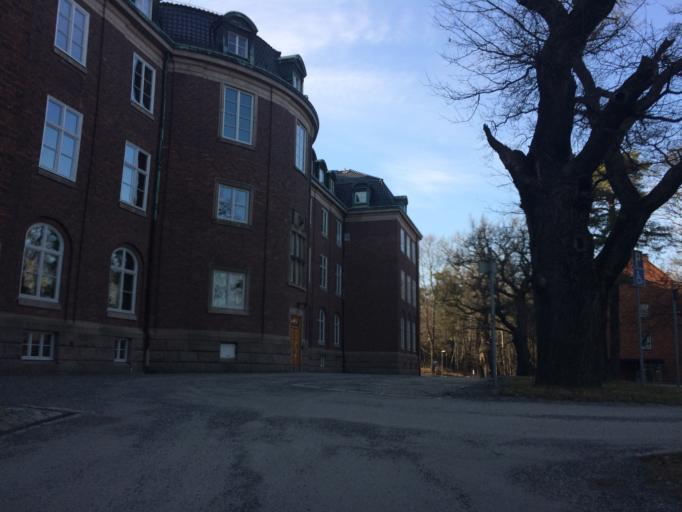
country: SE
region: Stockholm
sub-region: Norrtalje Kommun
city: Bergshamra
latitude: 59.3613
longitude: 18.0550
